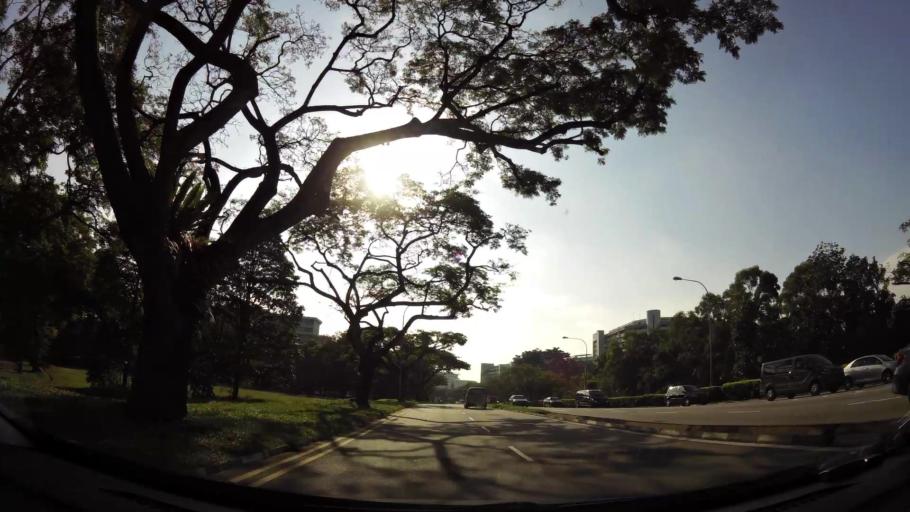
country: SG
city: Singapore
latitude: 1.3314
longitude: 103.9203
